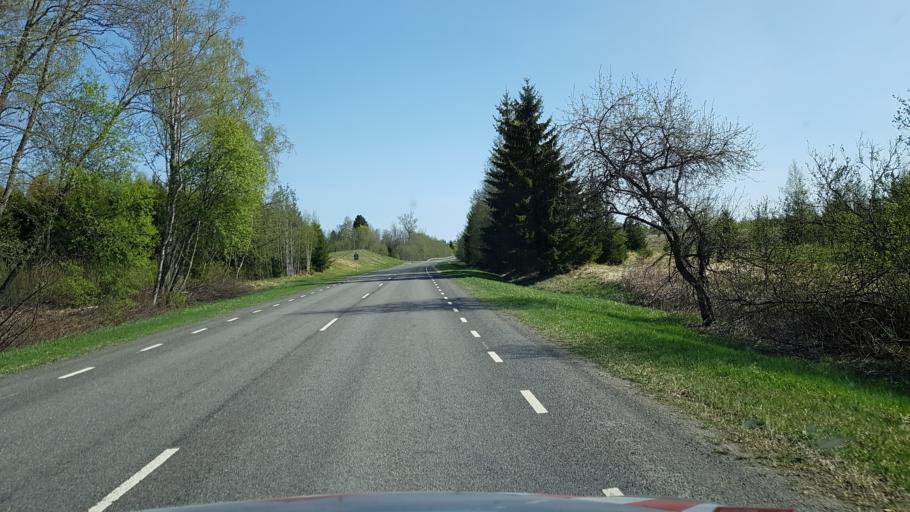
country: EE
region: Viljandimaa
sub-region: Karksi vald
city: Karksi-Nuia
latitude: 58.2330
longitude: 25.5821
